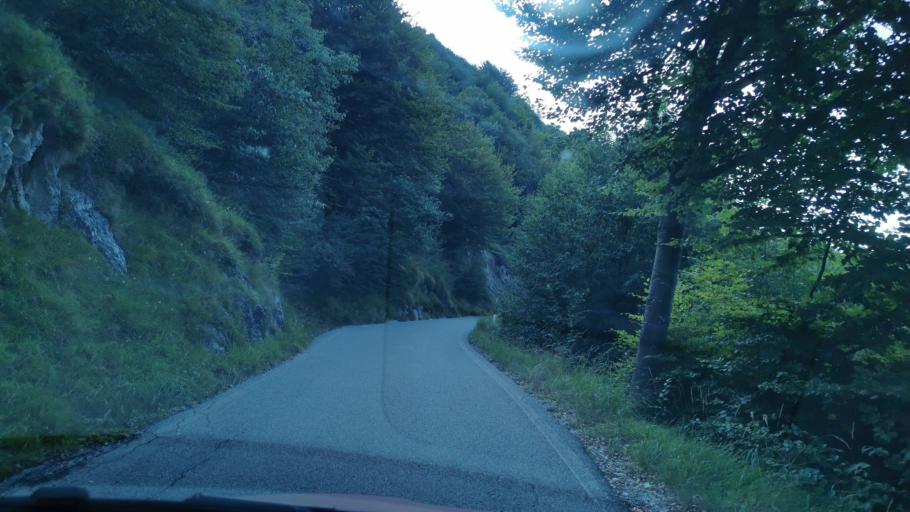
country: IT
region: Lombardy
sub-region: Provincia di Lecco
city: Moggio
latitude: 45.9191
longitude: 9.4915
